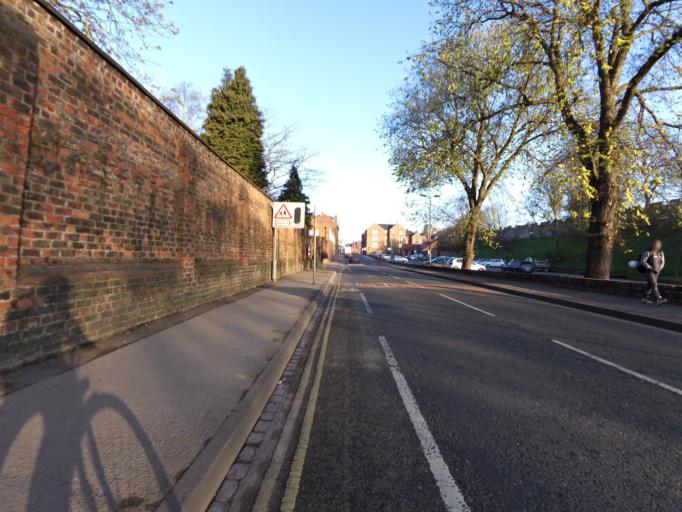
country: GB
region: England
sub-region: City of York
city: York
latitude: 53.9546
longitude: -1.0890
